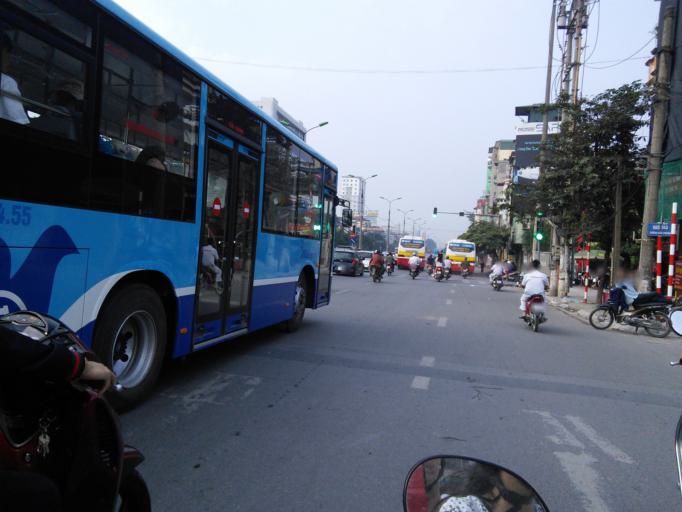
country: VN
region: Ha Noi
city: Hai BaTrung
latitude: 20.9916
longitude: 105.8413
